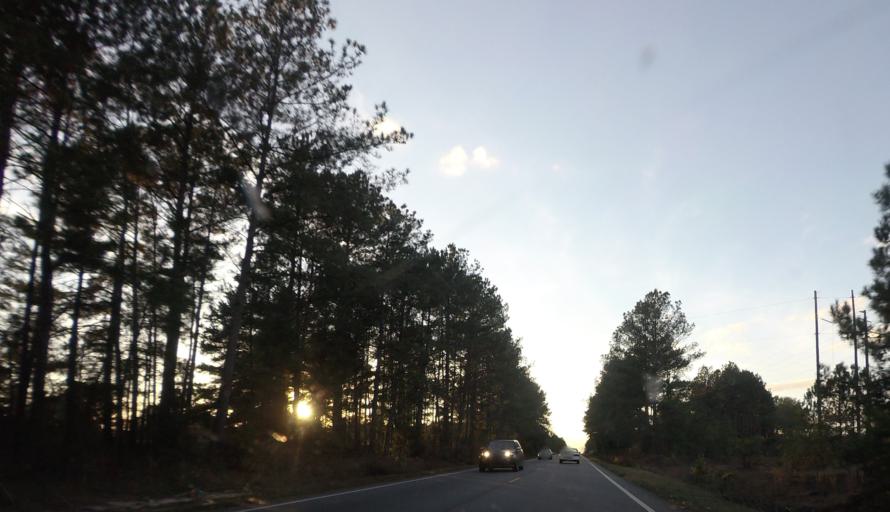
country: US
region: Georgia
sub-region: Houston County
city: Robins Air Force Base
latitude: 32.5434
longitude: -83.5568
